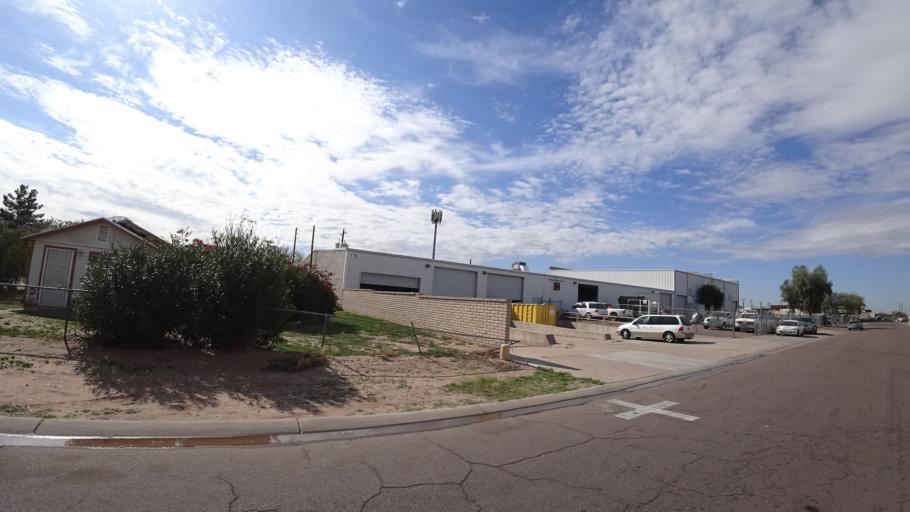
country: US
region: Arizona
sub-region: Maricopa County
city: Phoenix
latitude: 33.4175
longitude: -112.0698
